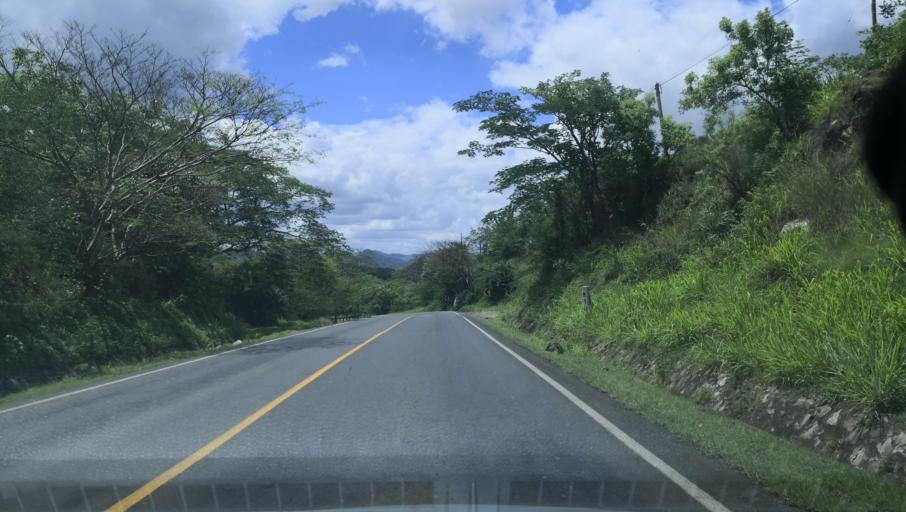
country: NI
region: Esteli
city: Condega
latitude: 13.3975
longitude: -86.3988
